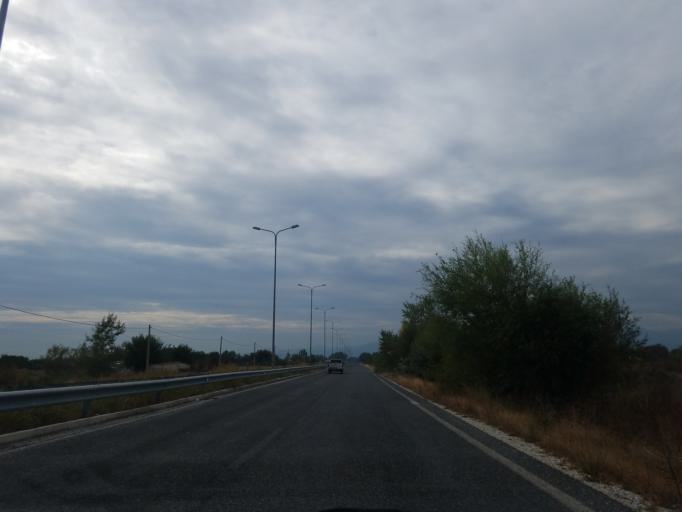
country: GR
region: Thessaly
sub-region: Trikala
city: Pyrgetos
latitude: 39.5558
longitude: 21.7337
